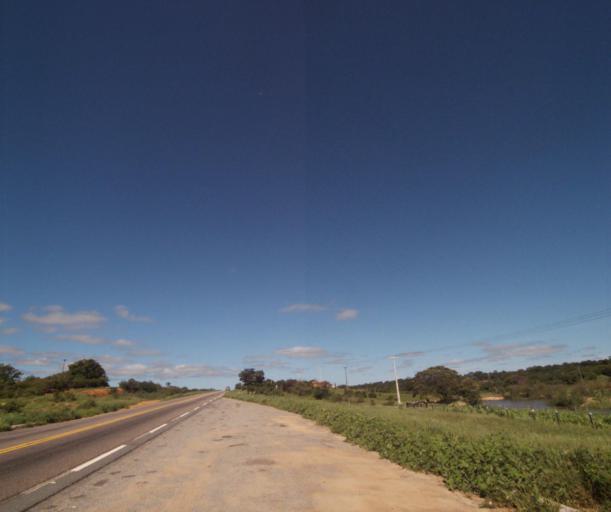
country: BR
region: Bahia
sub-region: Guanambi
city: Guanambi
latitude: -14.2326
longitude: -42.9545
